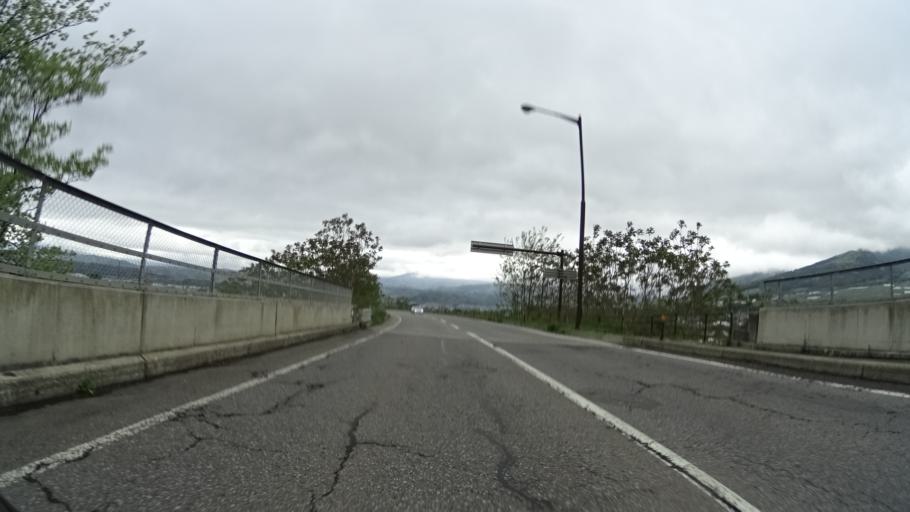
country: JP
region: Nagano
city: Nakano
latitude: 36.7592
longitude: 138.3896
